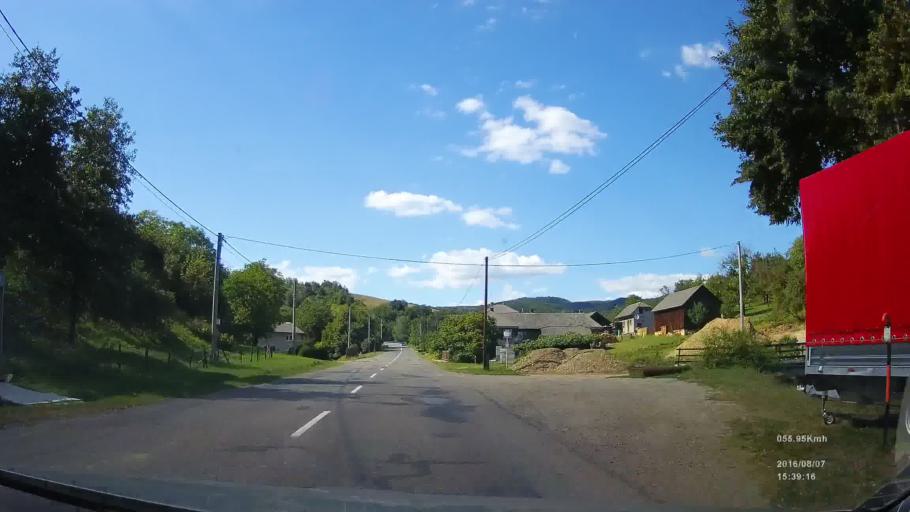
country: SK
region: Presovsky
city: Giraltovce
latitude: 49.1169
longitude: 21.6049
